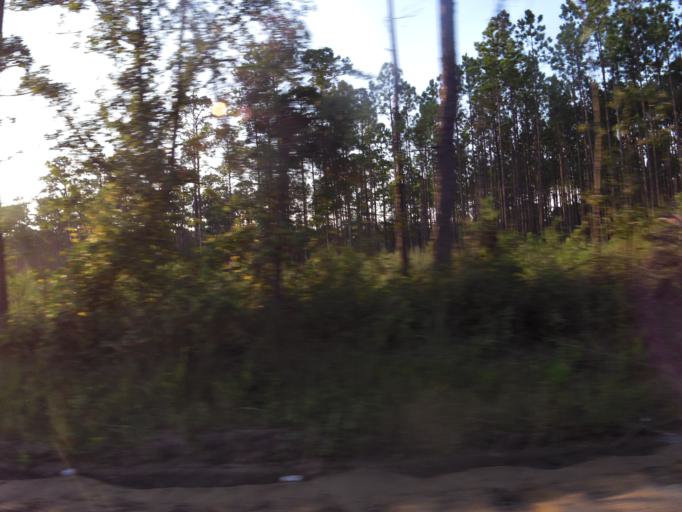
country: US
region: Florida
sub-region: Duval County
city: Baldwin
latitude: 30.3865
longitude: -82.0313
